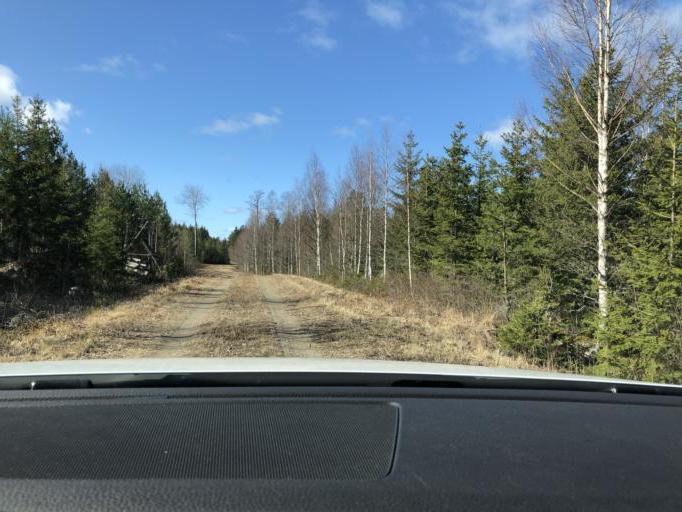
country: SE
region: Uppsala
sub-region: Heby Kommun
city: OEstervala
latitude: 60.2658
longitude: 17.1546
